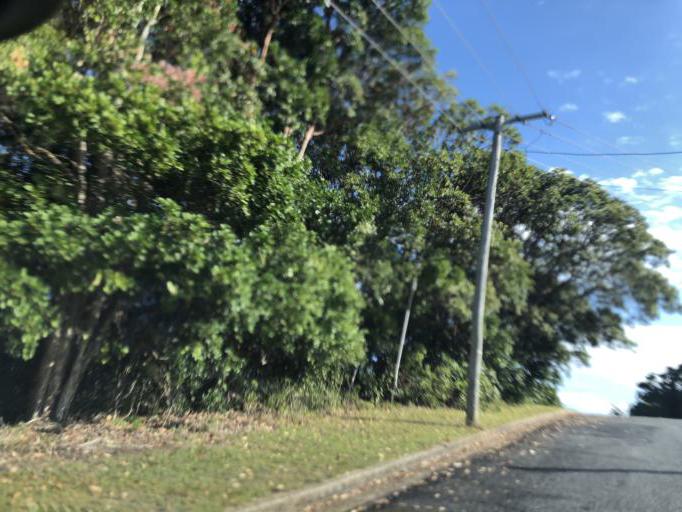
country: AU
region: New South Wales
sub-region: Coffs Harbour
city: Moonee Beach
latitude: -30.2371
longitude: 153.1509
